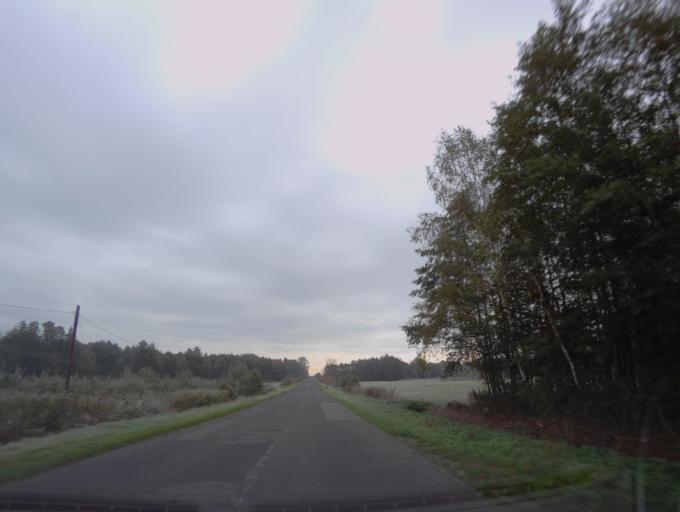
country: PL
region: Subcarpathian Voivodeship
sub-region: Powiat nizanski
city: Krzeszow
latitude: 50.4202
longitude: 22.3556
